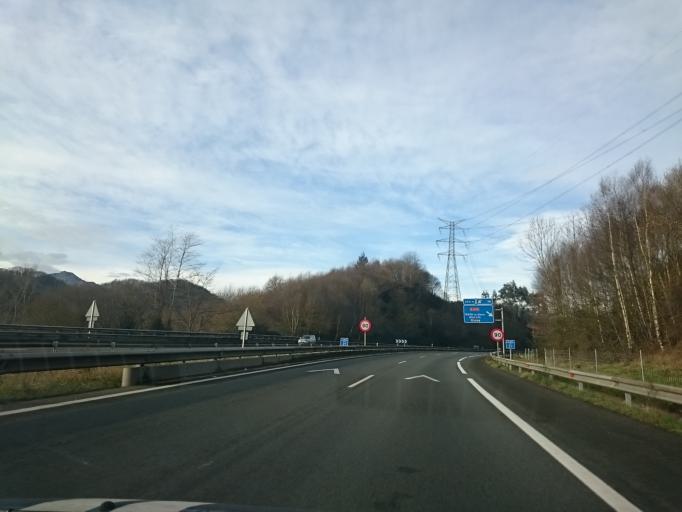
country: ES
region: Asturias
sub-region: Province of Asturias
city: Castandiello
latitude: 43.3108
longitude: -5.8674
